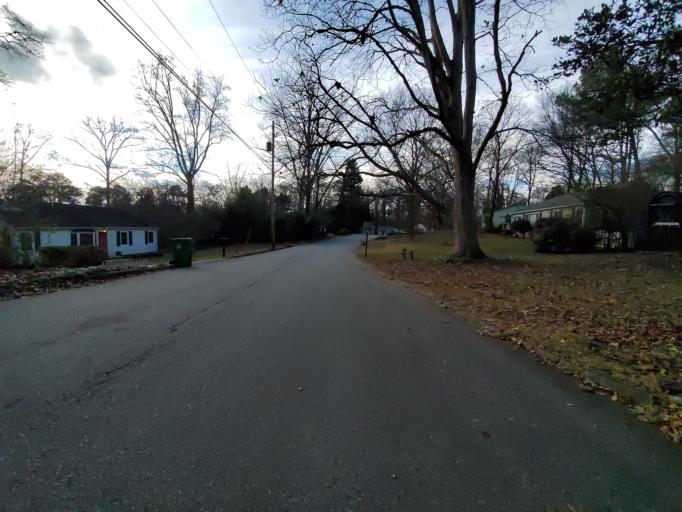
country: US
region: Georgia
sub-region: DeKalb County
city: North Decatur
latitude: 33.7974
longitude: -84.2961
